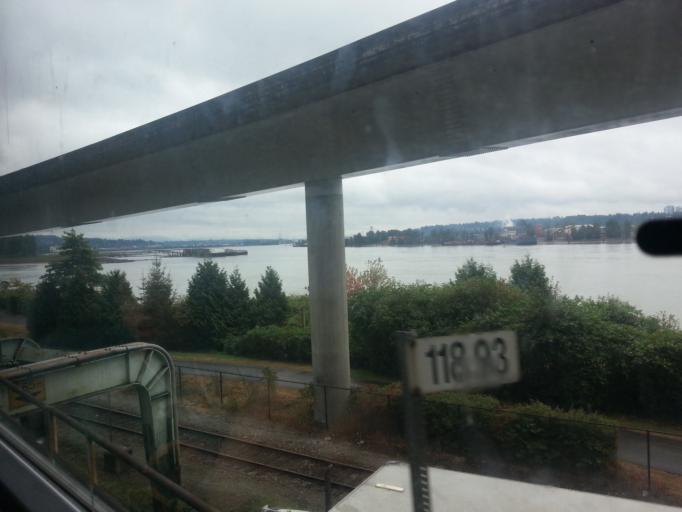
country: CA
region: British Columbia
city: New Westminster
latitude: 49.2125
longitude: -122.8955
